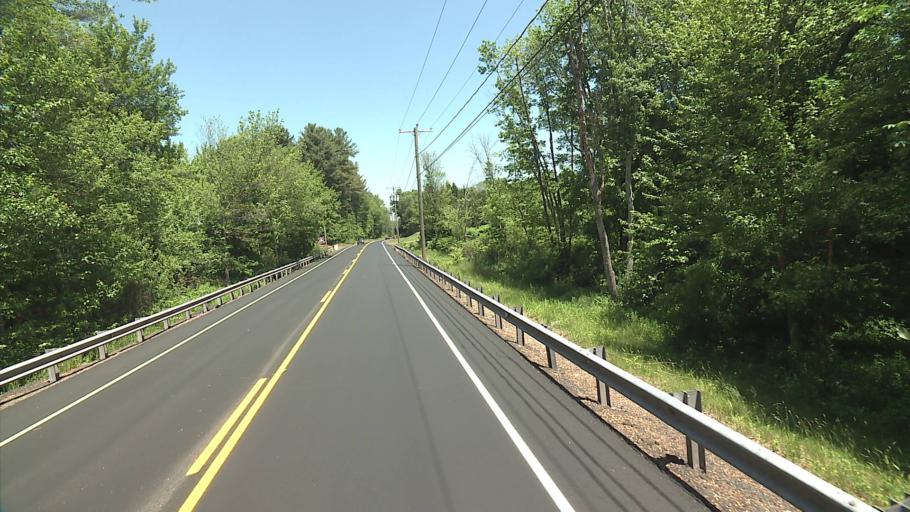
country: US
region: Connecticut
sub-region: Tolland County
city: Crystal Lake
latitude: 41.9329
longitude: -72.3821
